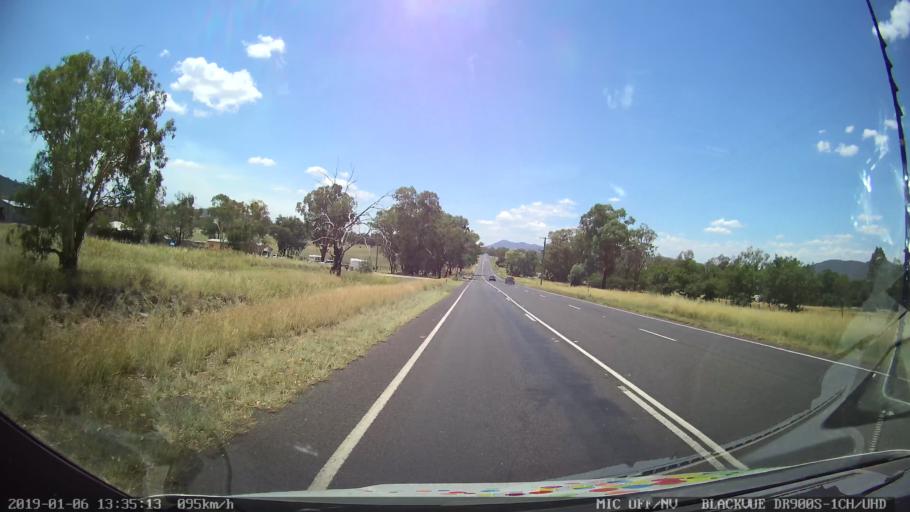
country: AU
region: New South Wales
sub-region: Tamworth Municipality
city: Kootingal
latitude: -31.0797
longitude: 151.0231
